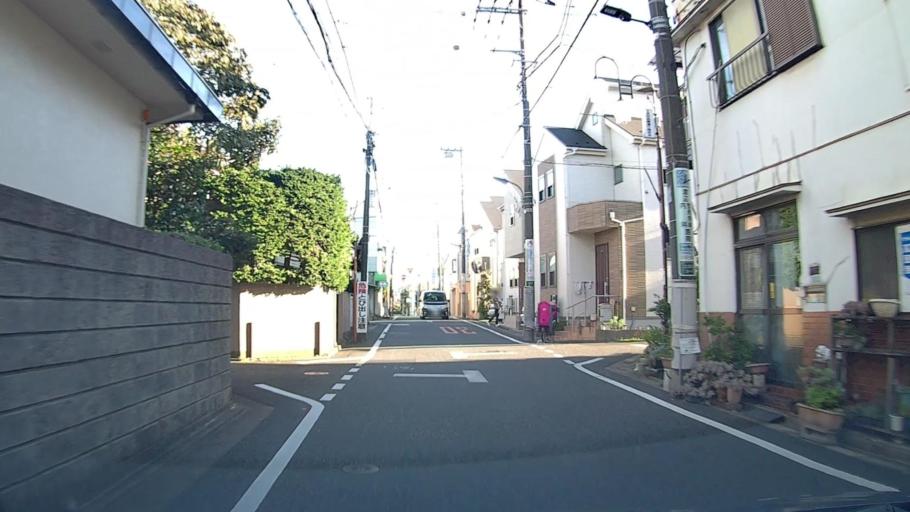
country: JP
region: Saitama
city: Wako
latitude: 35.7587
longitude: 139.6115
